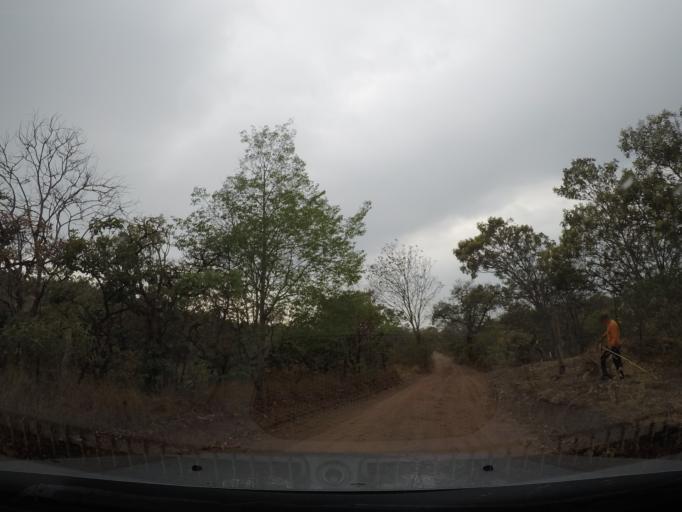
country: BR
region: Goias
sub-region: Pirenopolis
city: Pirenopolis
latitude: -15.8223
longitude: -48.8891
